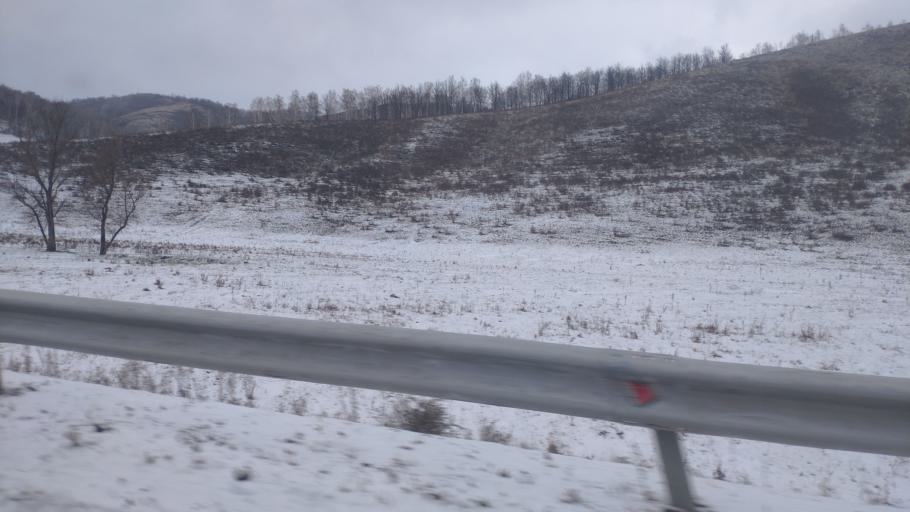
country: RU
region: Bashkortostan
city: Isyangulovo
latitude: 52.1617
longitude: 56.9099
